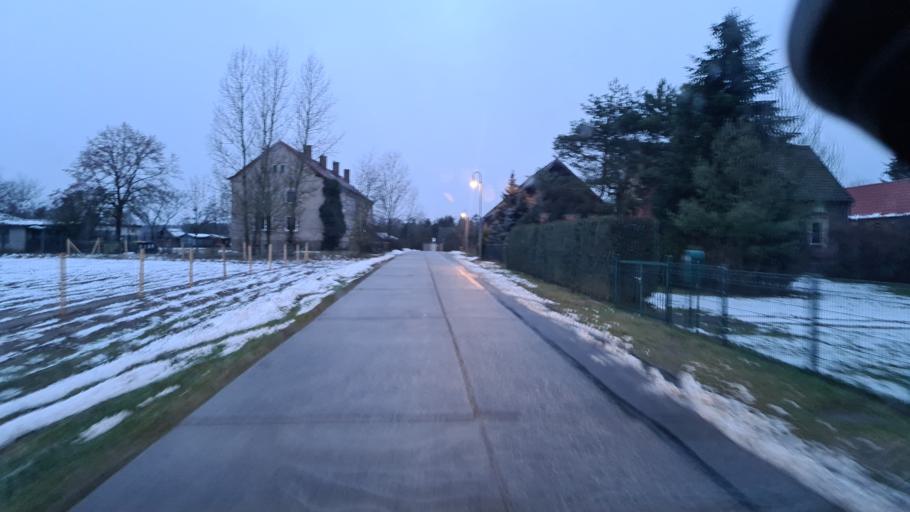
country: DE
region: Brandenburg
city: Schenkendobern
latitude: 51.9349
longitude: 14.5658
